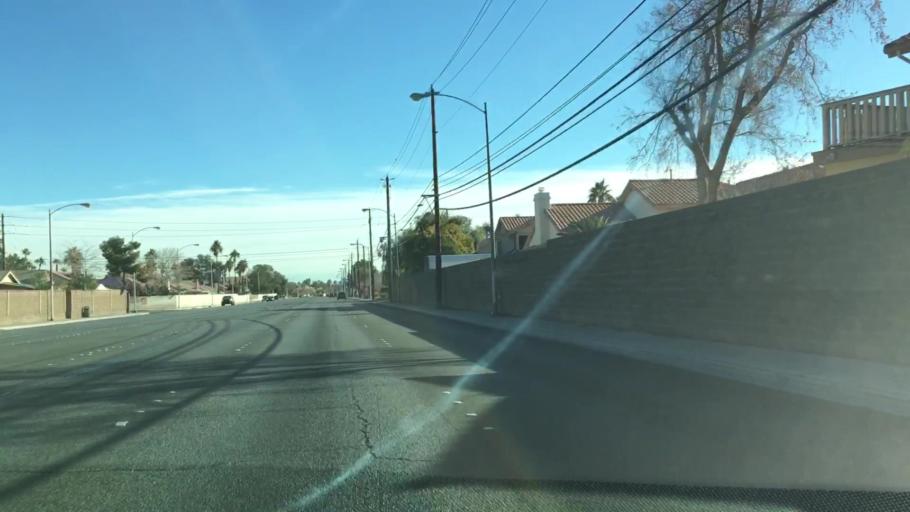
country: US
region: Nevada
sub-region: Clark County
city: Paradise
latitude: 36.0575
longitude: -115.1333
